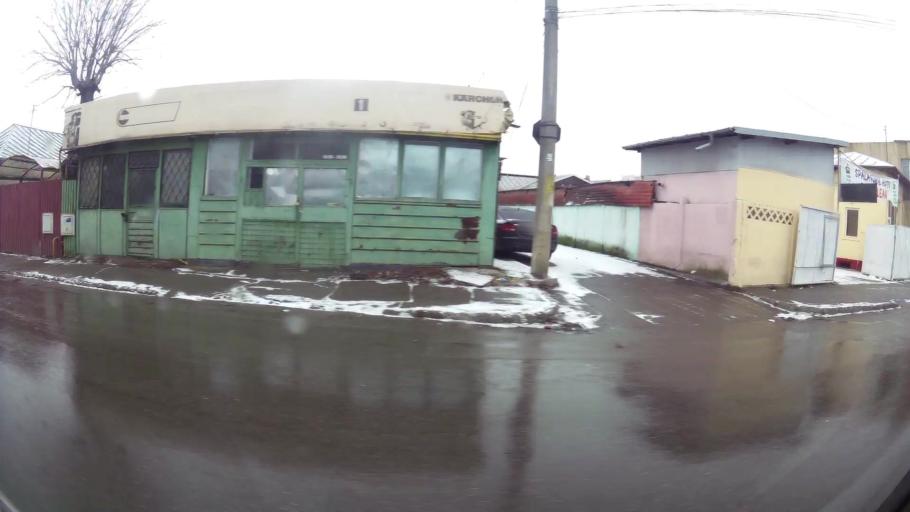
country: RO
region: Prahova
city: Ploiesti
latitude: 44.9534
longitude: 26.0174
